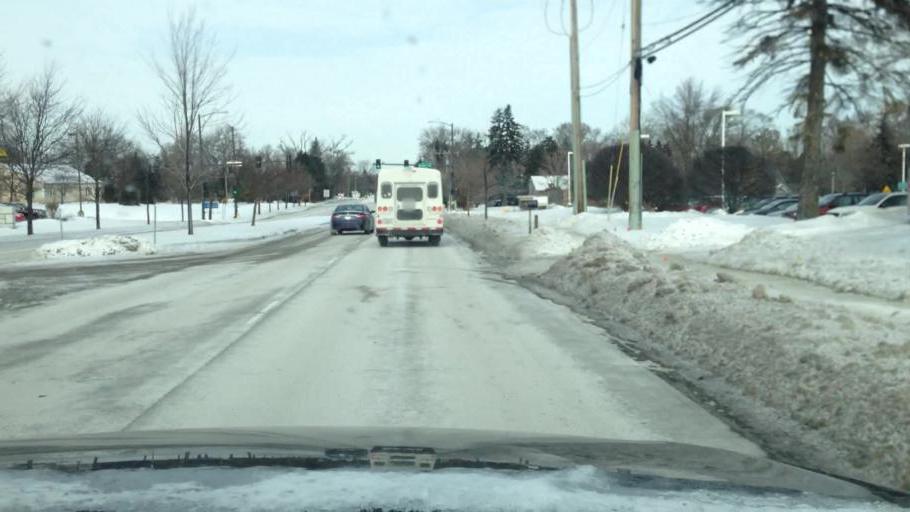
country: US
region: Illinois
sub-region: DuPage County
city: Lombard
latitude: 41.8491
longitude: -88.0117
